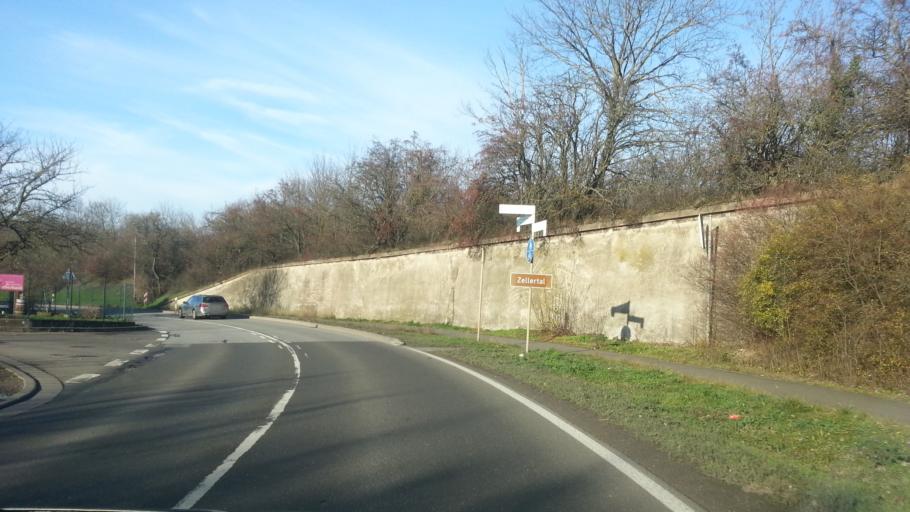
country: DE
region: Rheinland-Pfalz
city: Monsheim
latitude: 49.6346
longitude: 8.2025
